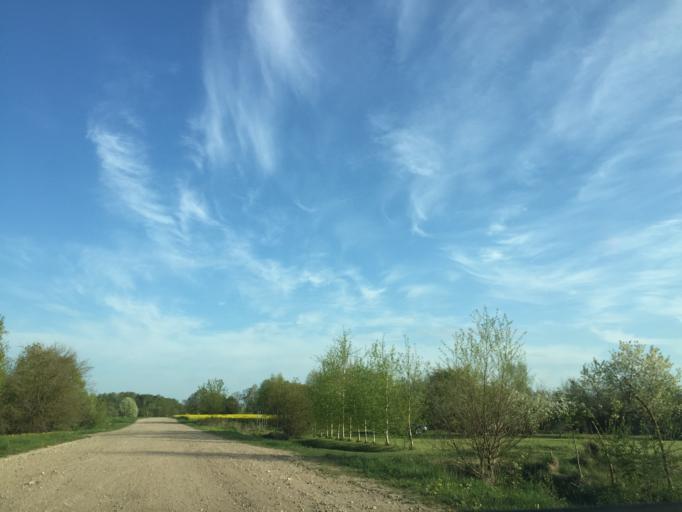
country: LV
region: Bauskas Rajons
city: Bauska
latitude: 56.3213
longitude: 24.2719
